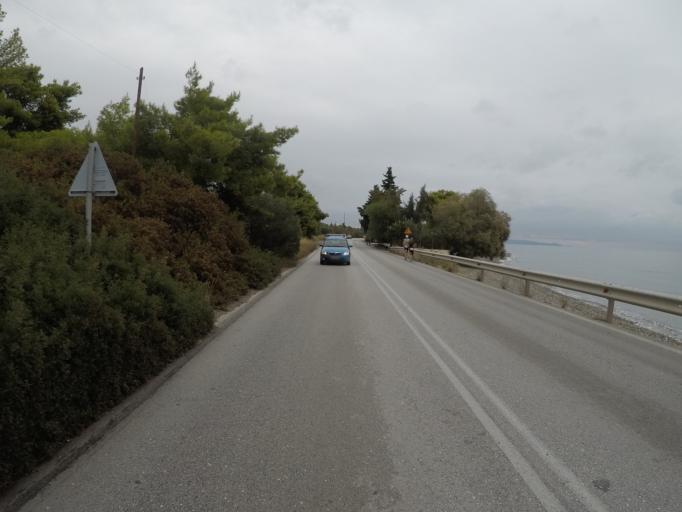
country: GR
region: Peloponnese
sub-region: Nomos Korinthias
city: Agioi Theodoroi
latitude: 37.9170
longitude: 23.1104
